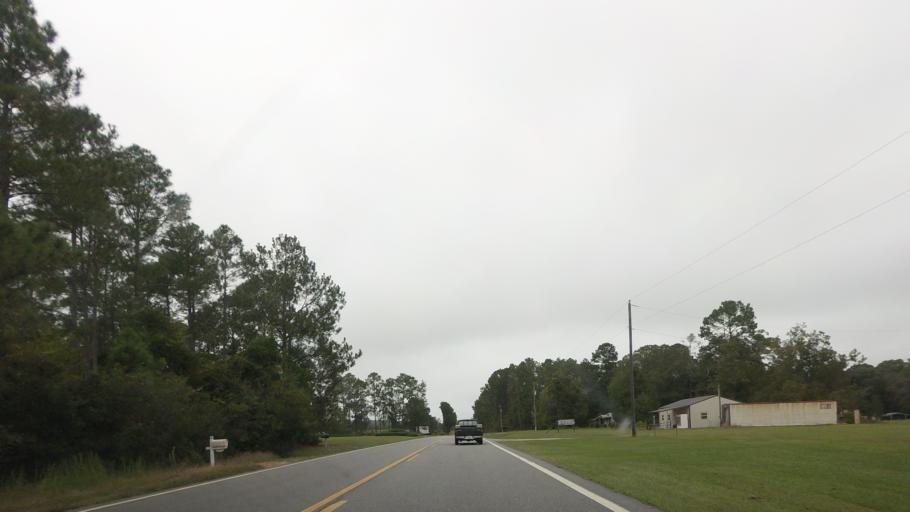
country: US
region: Georgia
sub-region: Berrien County
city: Enigma
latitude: 31.4223
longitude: -83.2457
